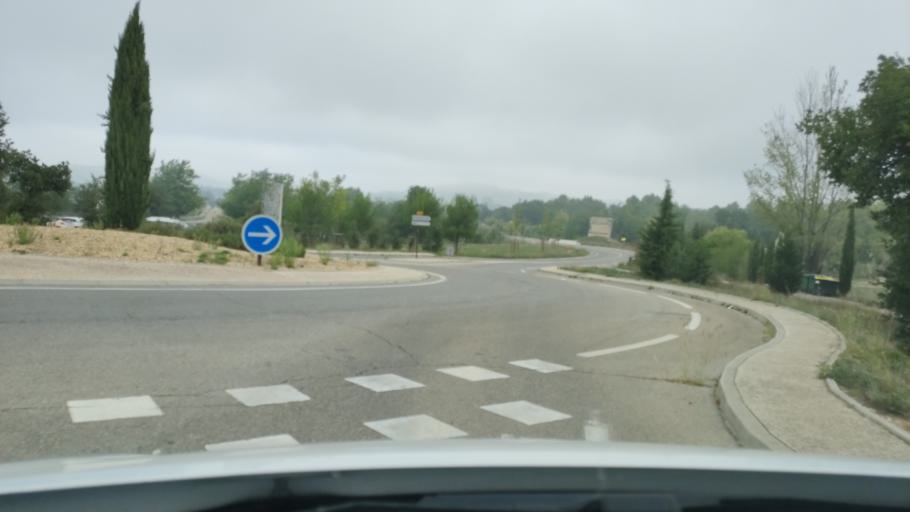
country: FR
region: Provence-Alpes-Cote d'Azur
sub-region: Departement du Vaucluse
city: Bonnieux
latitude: 43.8610
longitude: 5.3071
